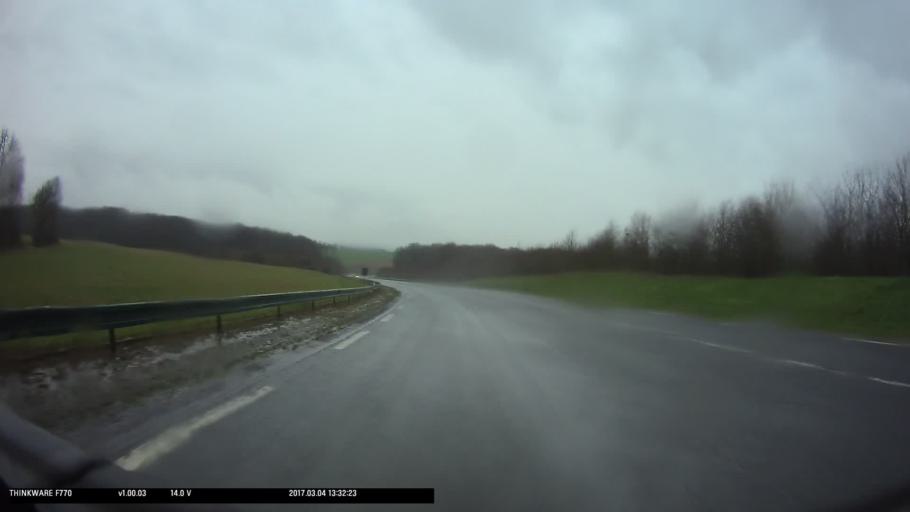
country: FR
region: Ile-de-France
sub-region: Departement du Val-d'Oise
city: Marines
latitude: 49.1325
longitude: 1.9900
